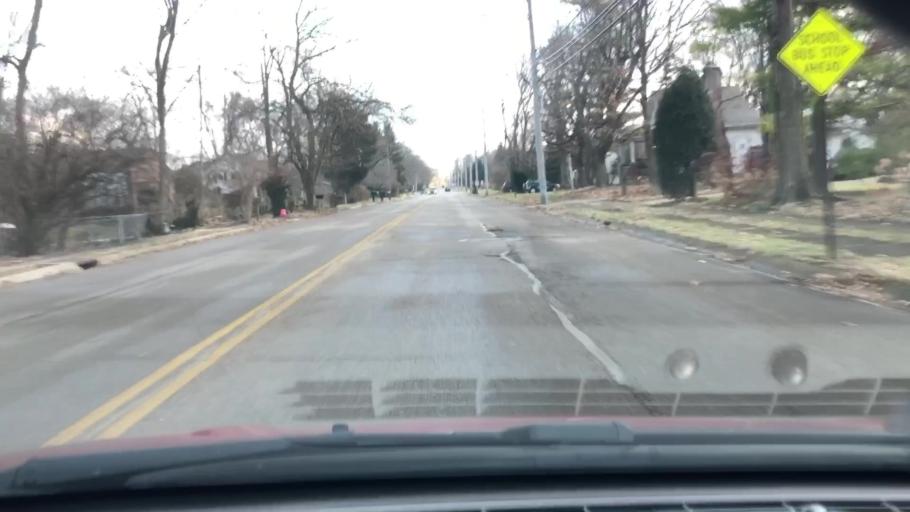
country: US
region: Ohio
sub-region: Greene County
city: Yellow Springs
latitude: 39.8039
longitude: -83.9031
